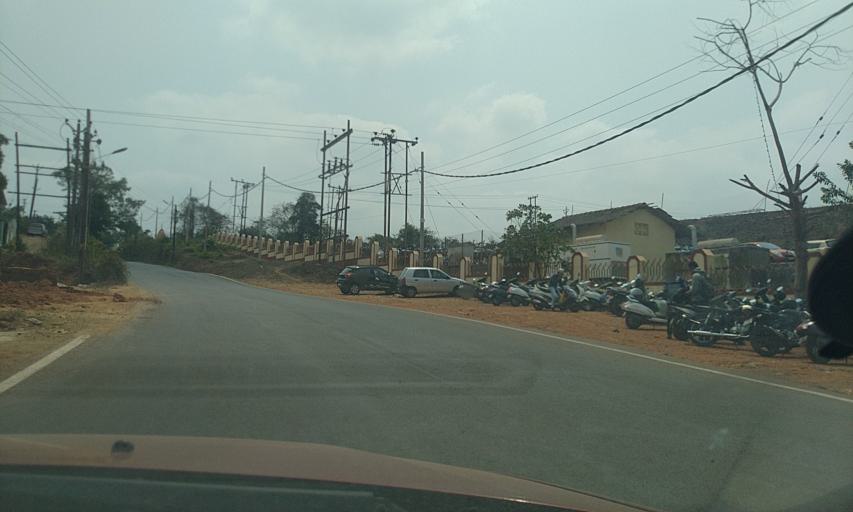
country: IN
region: Goa
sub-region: North Goa
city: Mapuca
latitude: 15.5953
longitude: 73.7954
